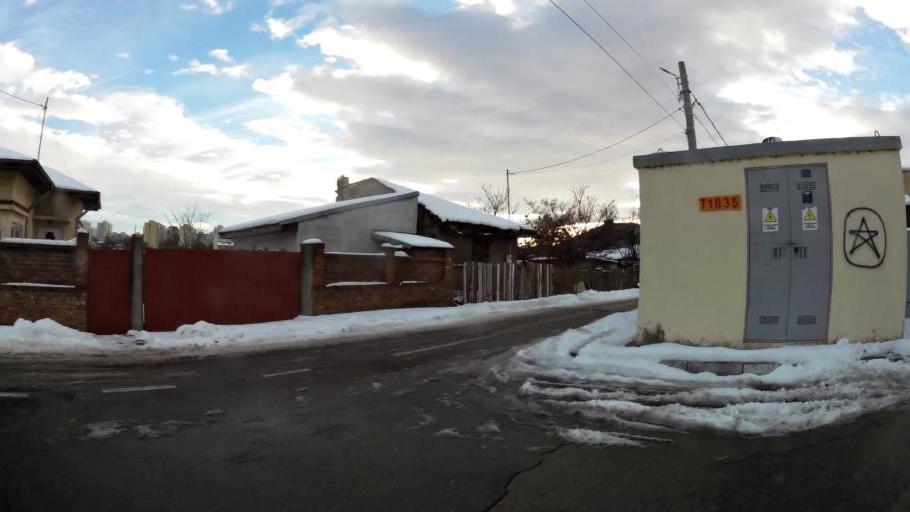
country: RO
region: Ilfov
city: Dobroesti
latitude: 44.4478
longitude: 26.1796
